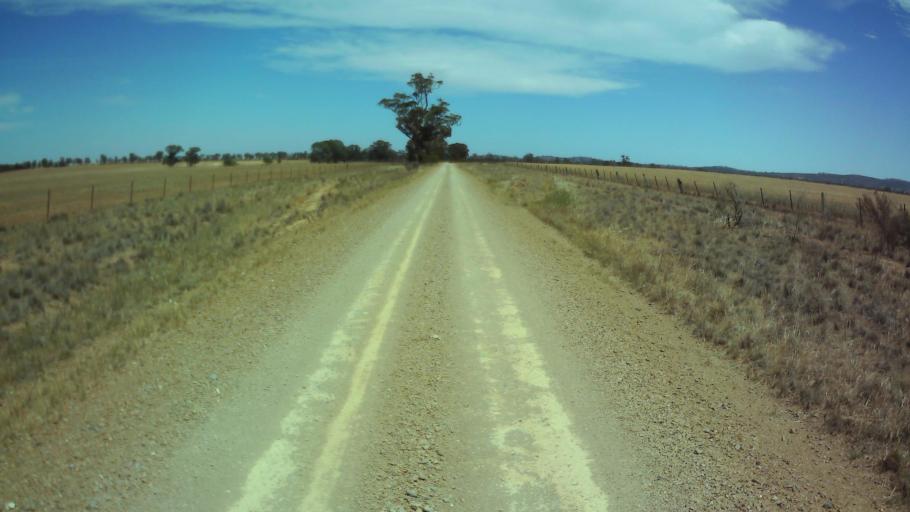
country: AU
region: New South Wales
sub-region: Weddin
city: Grenfell
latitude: -33.8581
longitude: 147.9198
